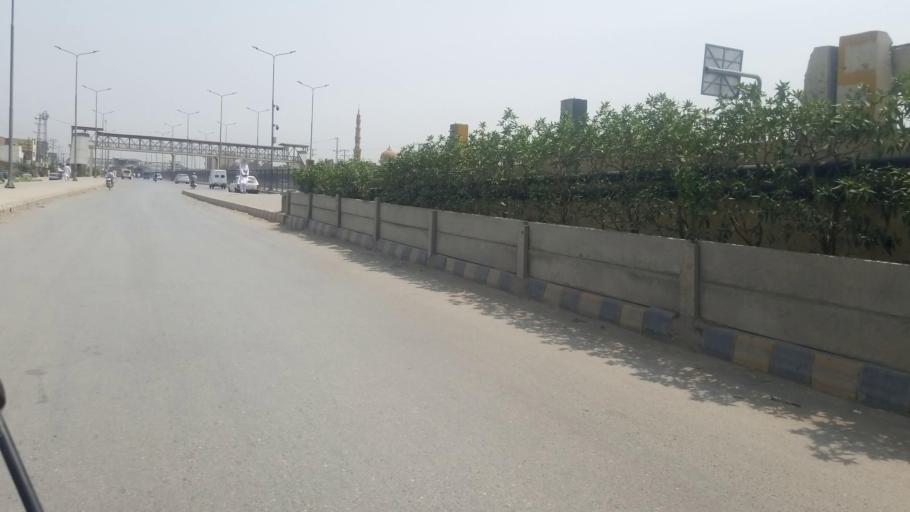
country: PK
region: Khyber Pakhtunkhwa
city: Peshawar
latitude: 34.0174
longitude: 71.6245
